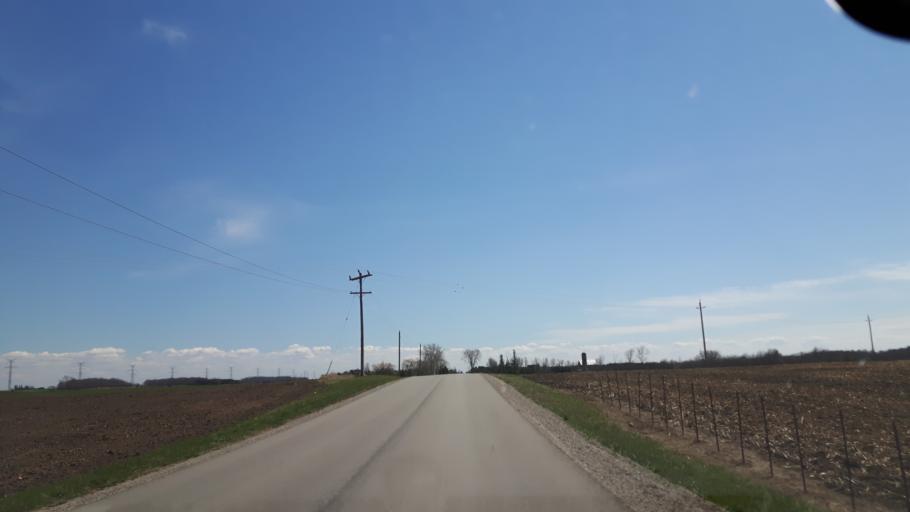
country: CA
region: Ontario
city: Goderich
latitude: 43.6201
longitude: -81.6440
